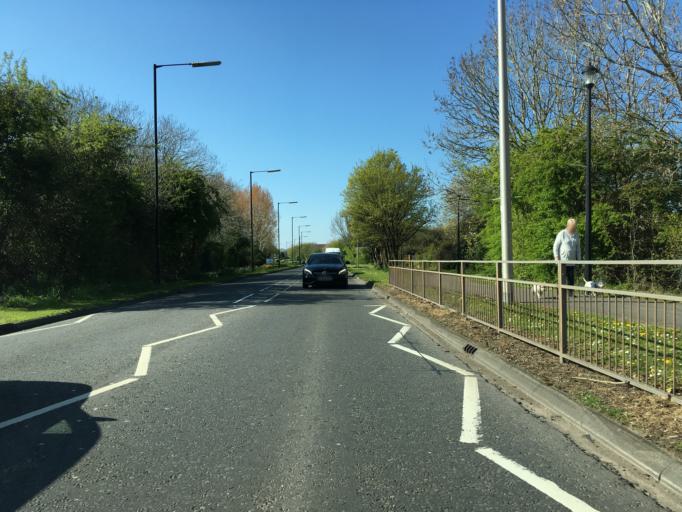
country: GB
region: England
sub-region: North Somerset
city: Portishead
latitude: 51.4785
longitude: -2.7561
